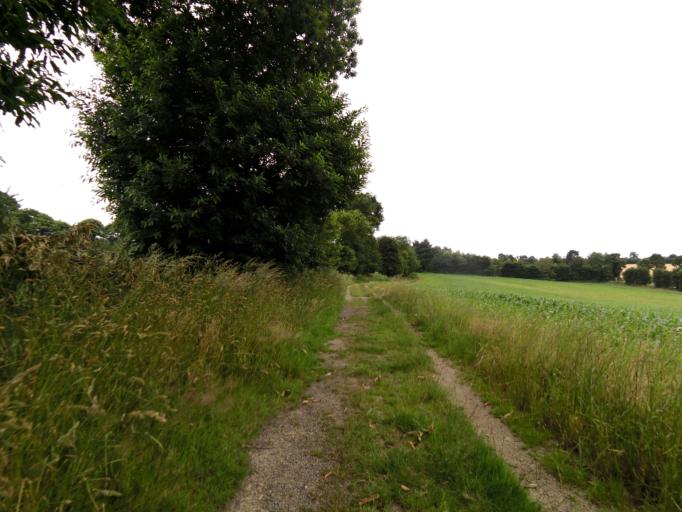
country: FR
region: Brittany
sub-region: Departement d'Ille-et-Vilaine
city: Chanteloup
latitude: 47.9308
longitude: -1.5970
